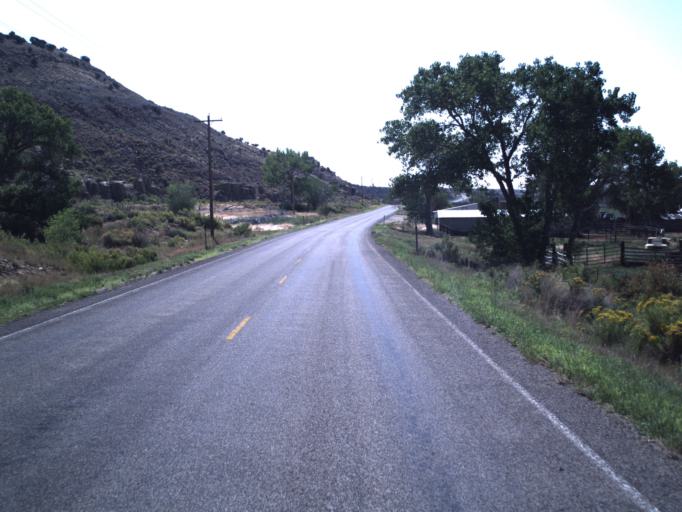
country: US
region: Utah
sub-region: Duchesne County
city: Duchesne
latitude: 40.2637
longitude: -110.4140
